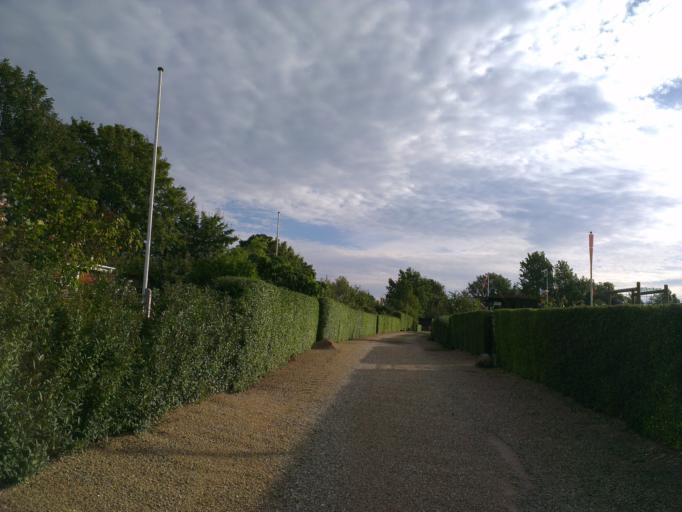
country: DK
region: Capital Region
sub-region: Frederikssund Kommune
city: Frederikssund
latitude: 55.8180
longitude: 12.0893
